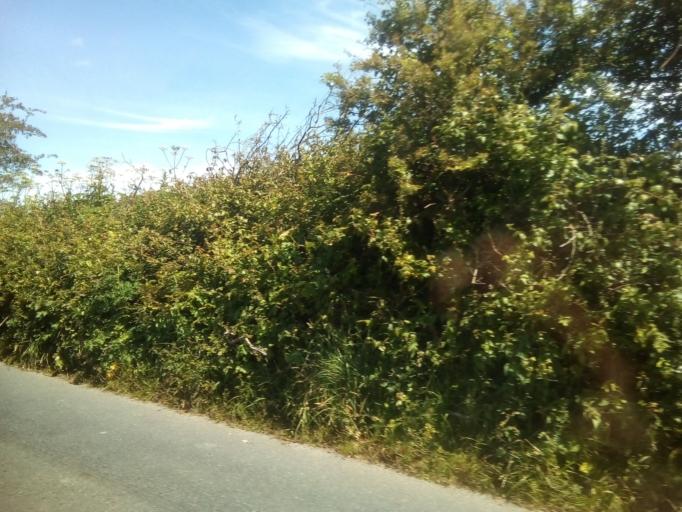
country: IE
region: Leinster
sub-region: Loch Garman
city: Loch Garman
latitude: 52.2579
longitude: -6.6171
